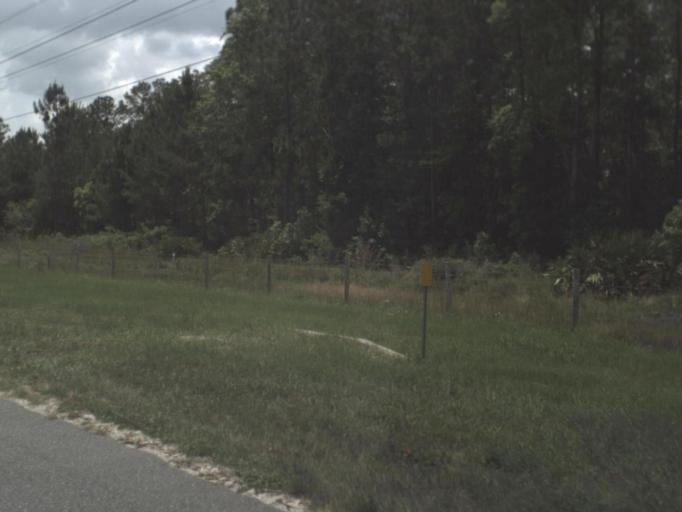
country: US
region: Florida
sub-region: Clay County
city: Keystone Heights
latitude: 29.8920
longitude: -81.9087
